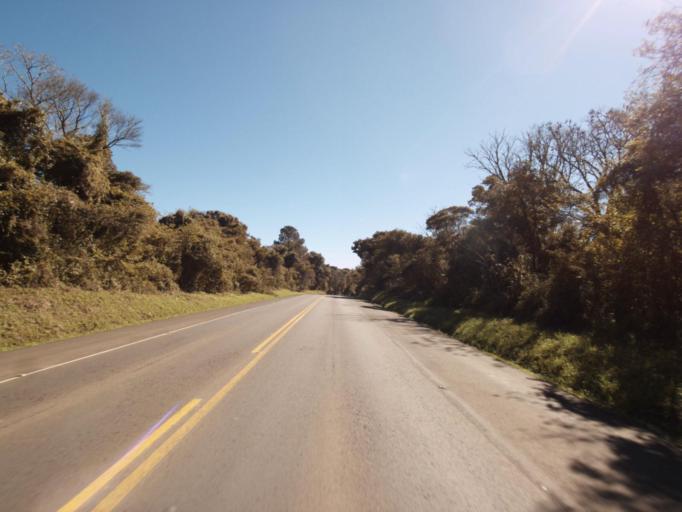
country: BR
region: Santa Catarina
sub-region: Joacaba
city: Joacaba
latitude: -27.1234
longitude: -51.6313
